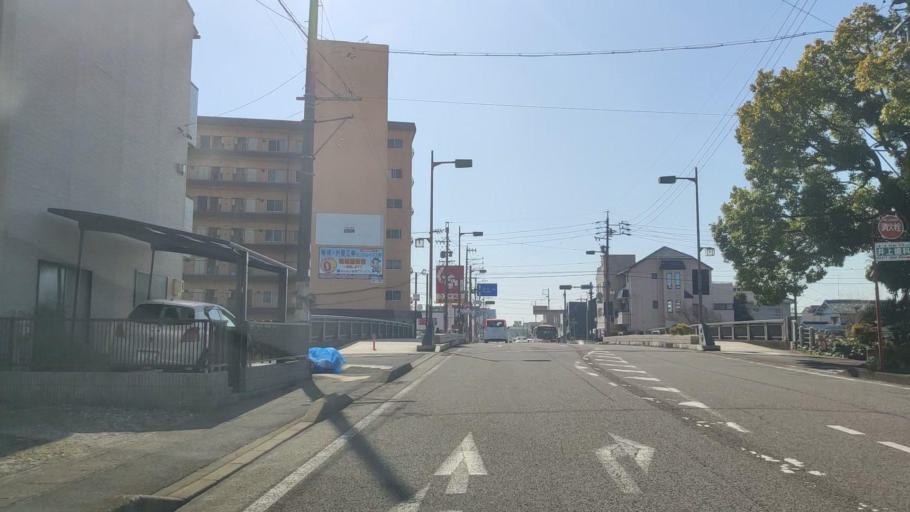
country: JP
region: Gifu
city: Gifu-shi
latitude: 35.4035
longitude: 136.7667
